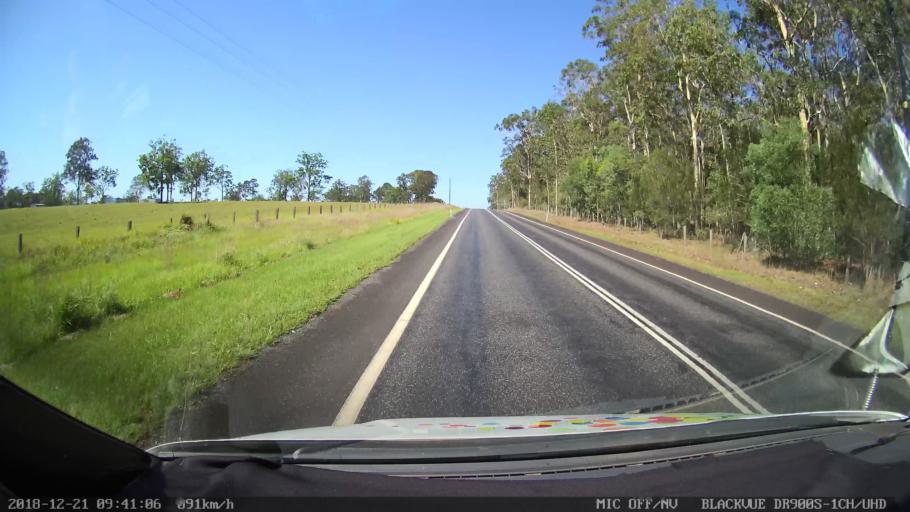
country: AU
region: New South Wales
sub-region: Clarence Valley
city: Grafton
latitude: -29.5813
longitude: 152.9604
